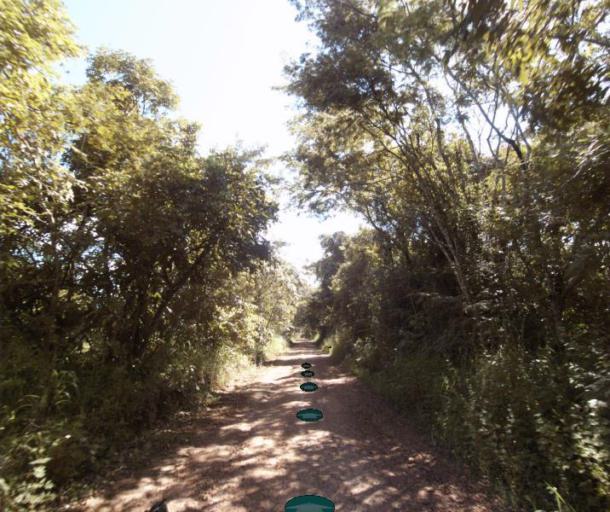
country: BR
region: Goias
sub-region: Pirenopolis
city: Pirenopolis
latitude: -15.7743
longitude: -49.0234
